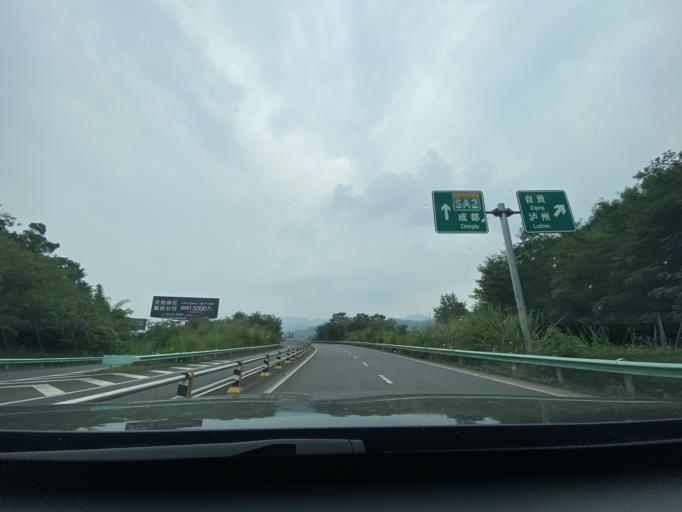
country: CN
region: Sichuan
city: Wenlin
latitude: 30.2948
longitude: 104.1220
